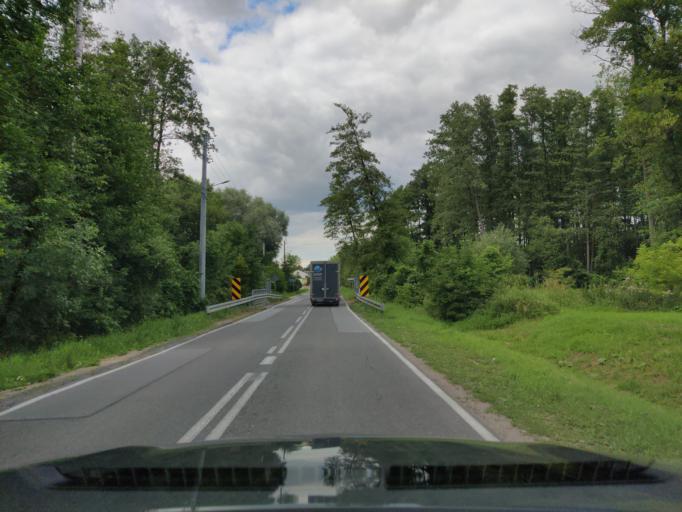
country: PL
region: Masovian Voivodeship
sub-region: Powiat sokolowski
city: Kosow Lacki
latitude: 52.5848
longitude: 22.1535
